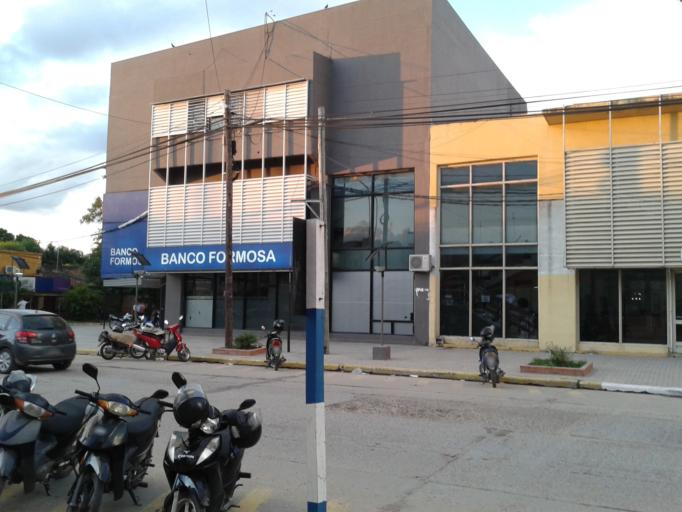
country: AR
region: Formosa
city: Clorinda
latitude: -25.2869
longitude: -57.7137
